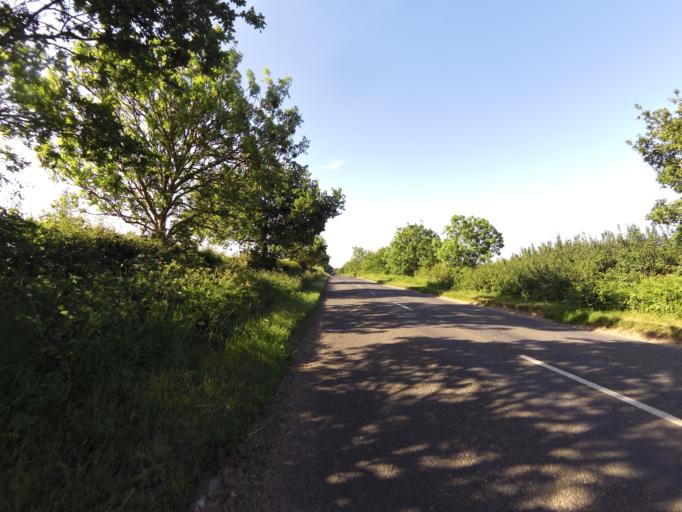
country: GB
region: England
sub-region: Suffolk
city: Woodbridge
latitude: 52.0733
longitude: 1.3630
